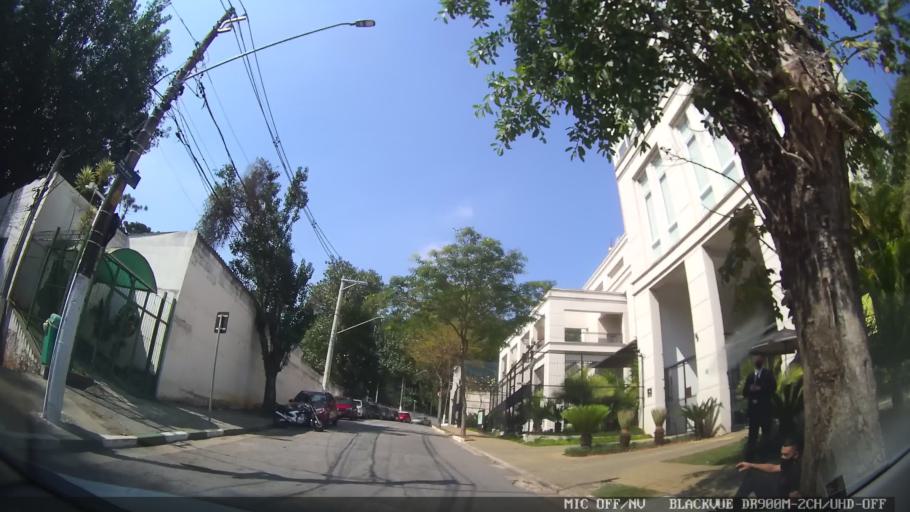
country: BR
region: Sao Paulo
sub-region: Sao Paulo
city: Sao Paulo
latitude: -23.4868
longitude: -46.6323
